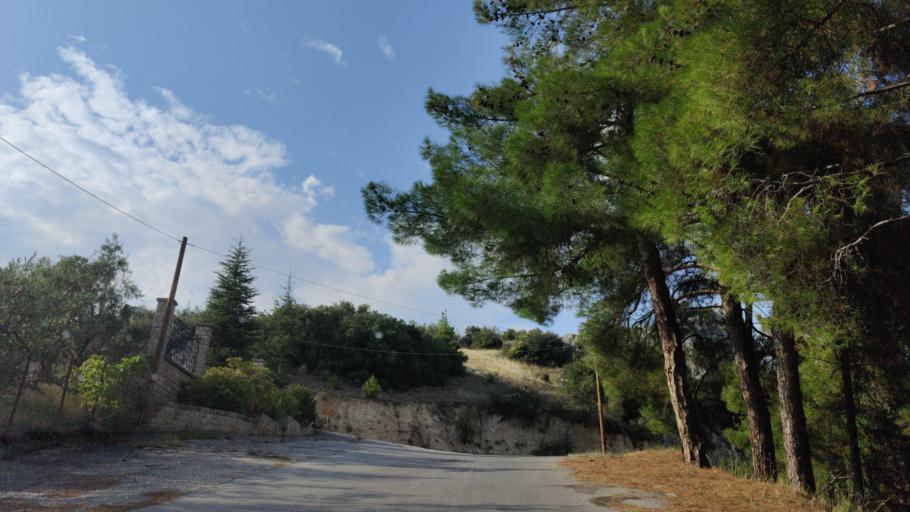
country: GR
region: Central Macedonia
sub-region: Nomos Serron
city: Sidirokastro
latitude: 41.2358
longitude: 23.4003
